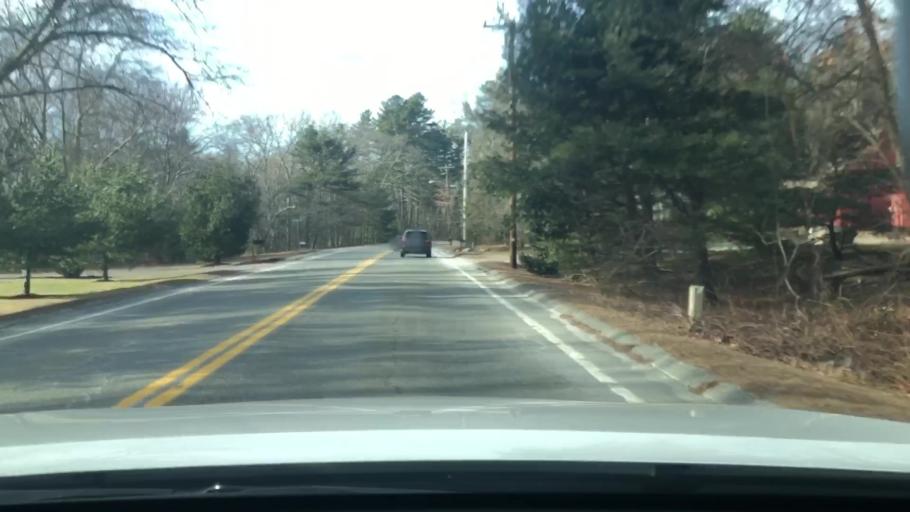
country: US
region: Massachusetts
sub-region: Worcester County
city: Northbridge
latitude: 42.1766
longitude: -71.6363
